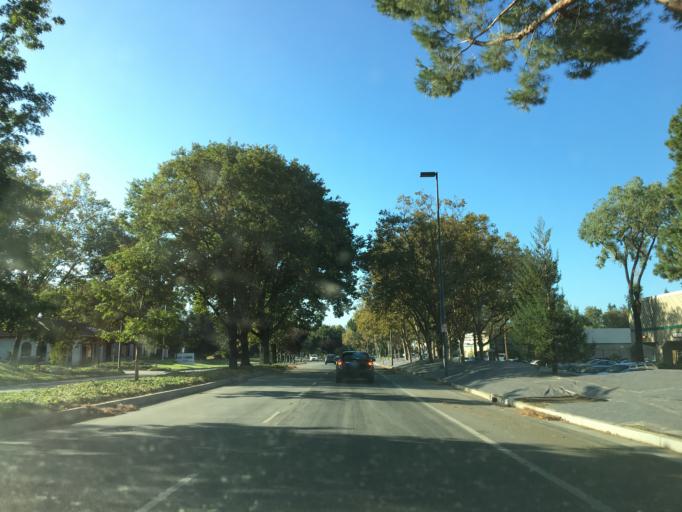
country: US
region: California
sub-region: Santa Clara County
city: Milpitas
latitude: 37.3956
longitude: -121.8910
